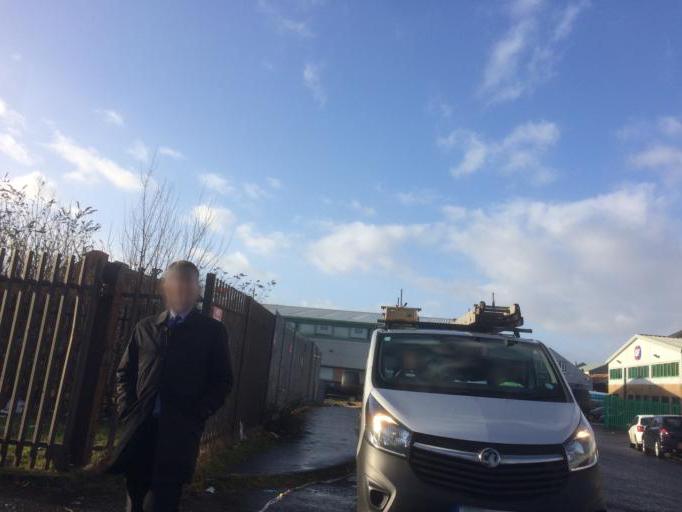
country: GB
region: Scotland
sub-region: Glasgow City
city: Glasgow
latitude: 55.8522
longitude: -4.2760
